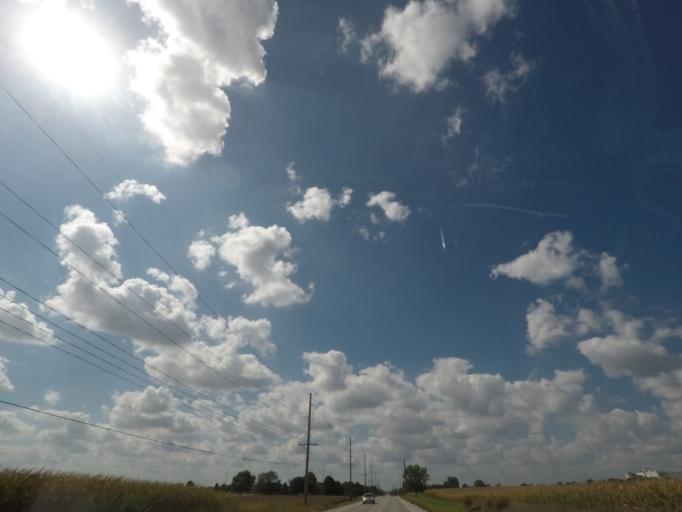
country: US
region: Iowa
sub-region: Story County
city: Ames
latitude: 42.0231
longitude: -93.5548
